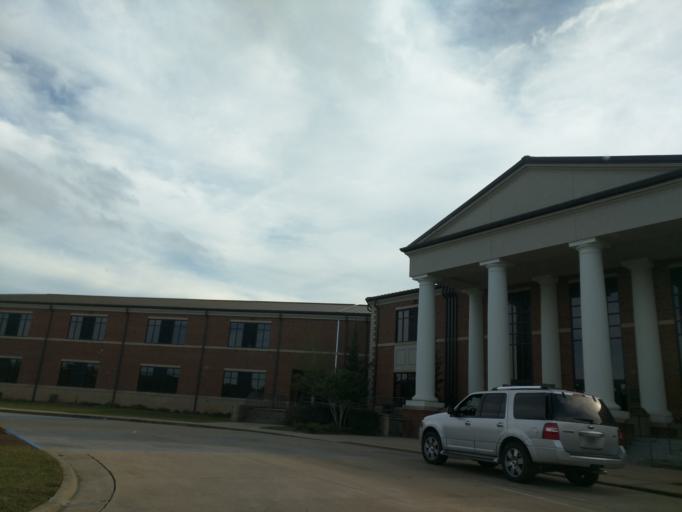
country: US
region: Georgia
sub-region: Decatur County
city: Bainbridge
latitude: 30.8867
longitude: -84.4811
